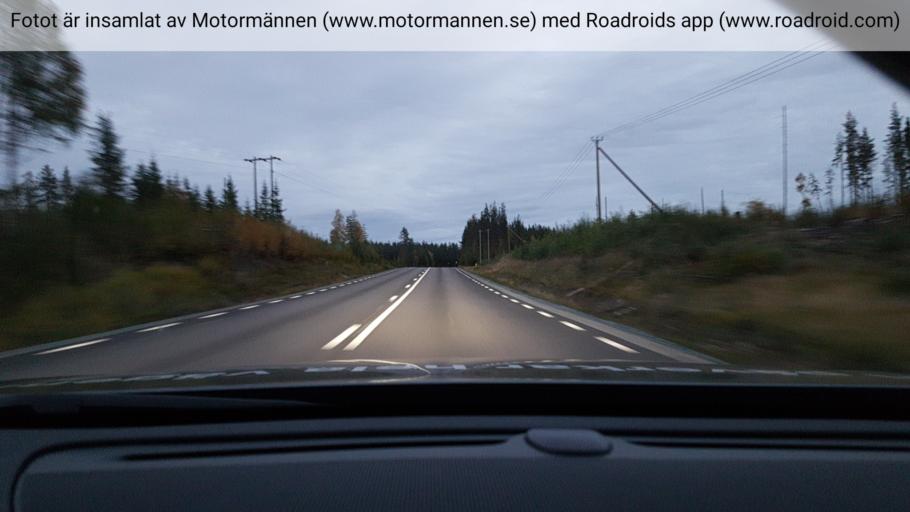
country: SE
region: Norrbotten
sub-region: Alvsbyns Kommun
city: AElvsbyn
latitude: 65.7449
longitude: 20.9436
